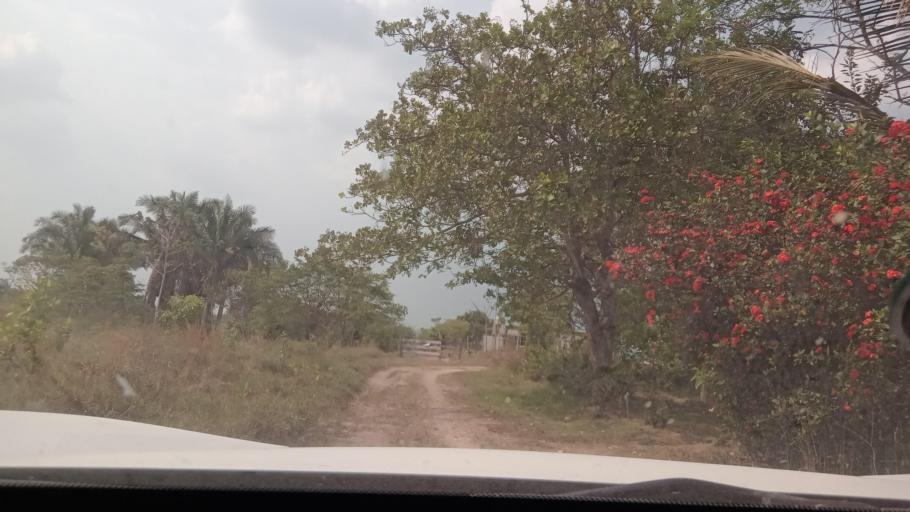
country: MX
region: Tabasco
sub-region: Huimanguillo
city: Francisco Rueda
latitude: 17.6928
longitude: -93.8328
